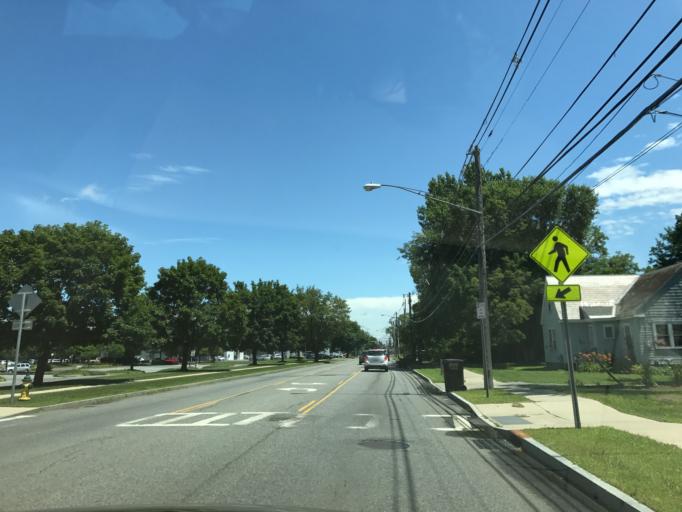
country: US
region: New York
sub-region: Warren County
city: Glens Falls
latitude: 43.3030
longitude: -73.6613
